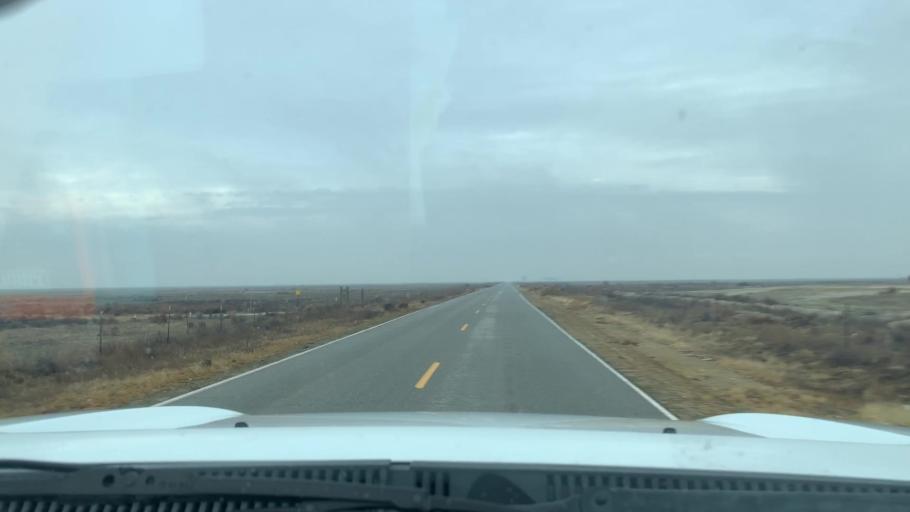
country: US
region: California
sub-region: Kern County
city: Lost Hills
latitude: 35.6442
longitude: -119.5801
